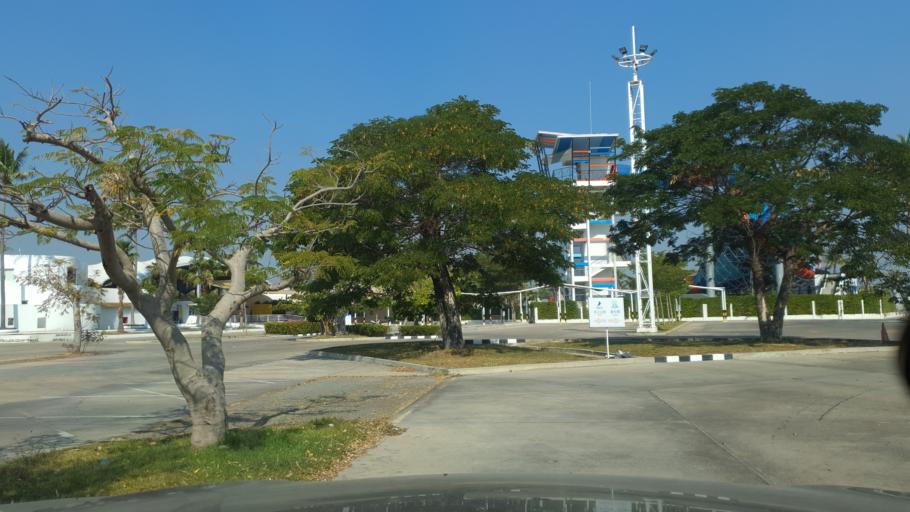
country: TH
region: Phetchaburi
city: Cha-am
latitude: 12.8307
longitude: 99.9322
